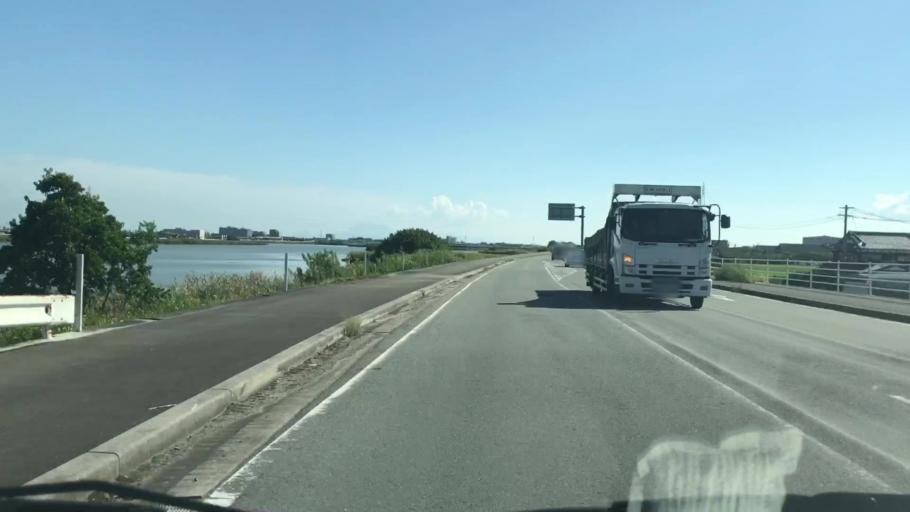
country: JP
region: Saga Prefecture
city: Okawa
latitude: 33.2360
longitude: 130.3800
